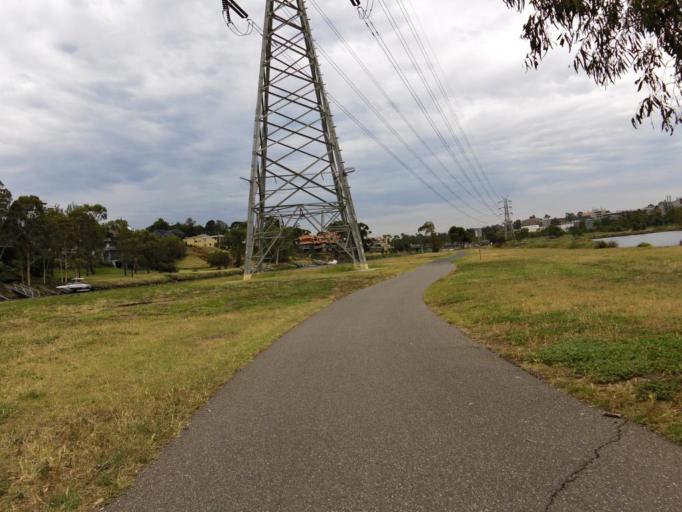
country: AU
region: Victoria
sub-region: Melbourne
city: Ascot Vale
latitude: -37.7856
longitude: 144.9034
